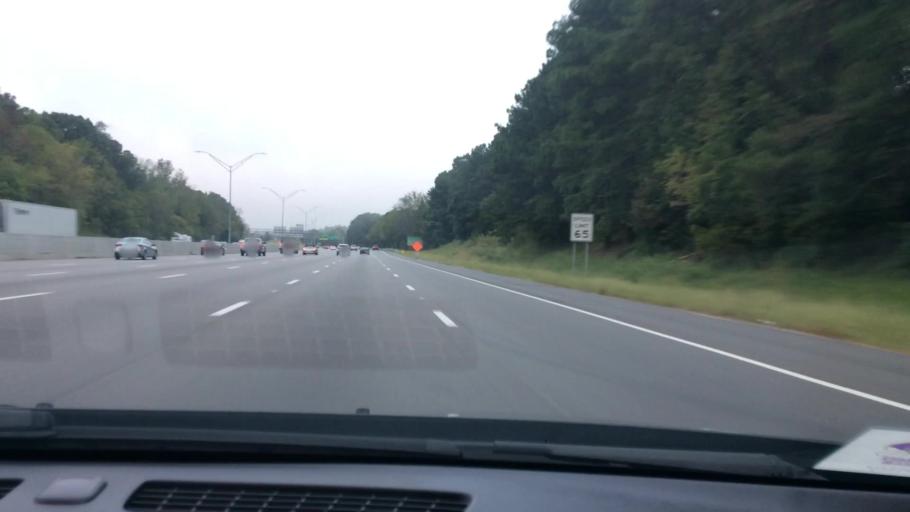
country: US
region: North Carolina
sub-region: Wake County
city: Raleigh
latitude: 35.7570
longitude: -78.6034
